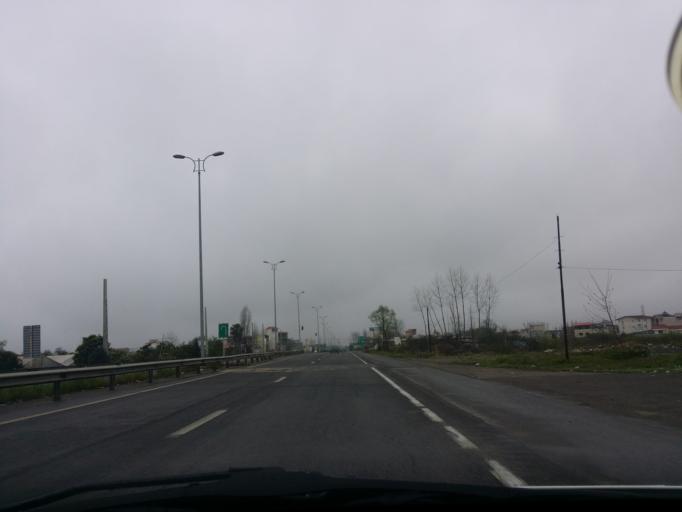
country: IR
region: Mazandaran
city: Tonekabon
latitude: 36.8004
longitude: 50.8891
